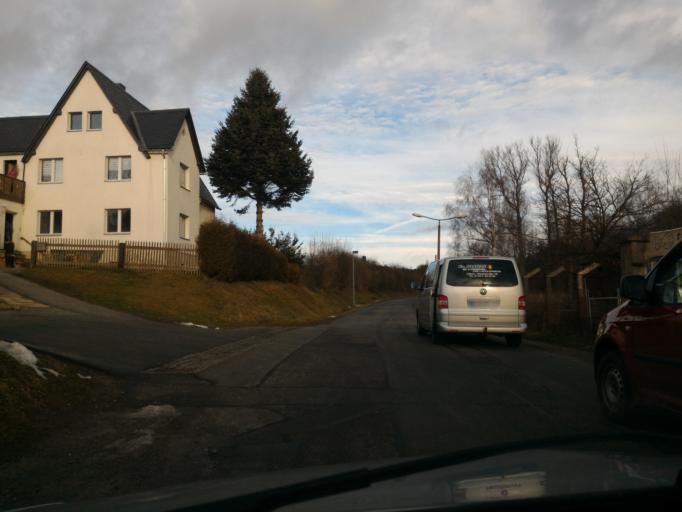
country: DE
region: Saxony
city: Oppach
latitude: 51.0646
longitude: 14.5001
